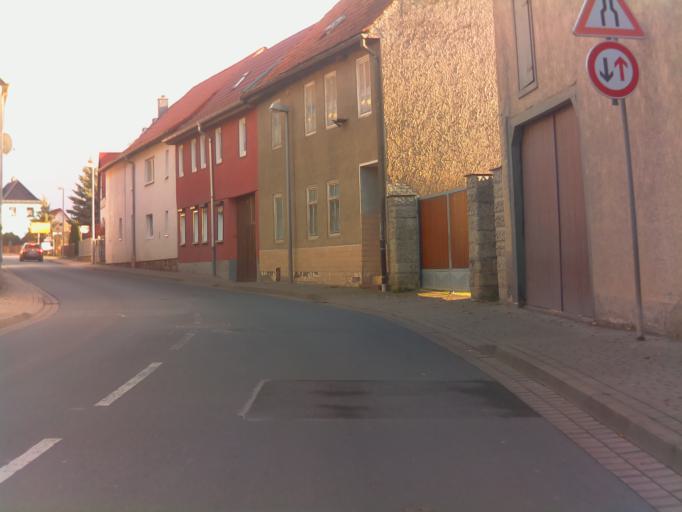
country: DE
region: Thuringia
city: Rittersdorf
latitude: 50.8580
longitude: 11.2491
